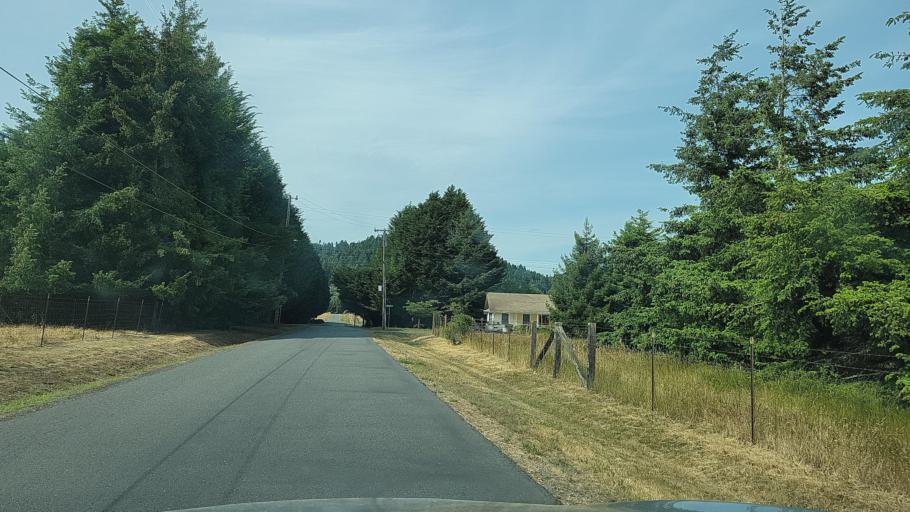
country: US
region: California
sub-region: Humboldt County
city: Hydesville
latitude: 40.5479
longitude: -124.0767
